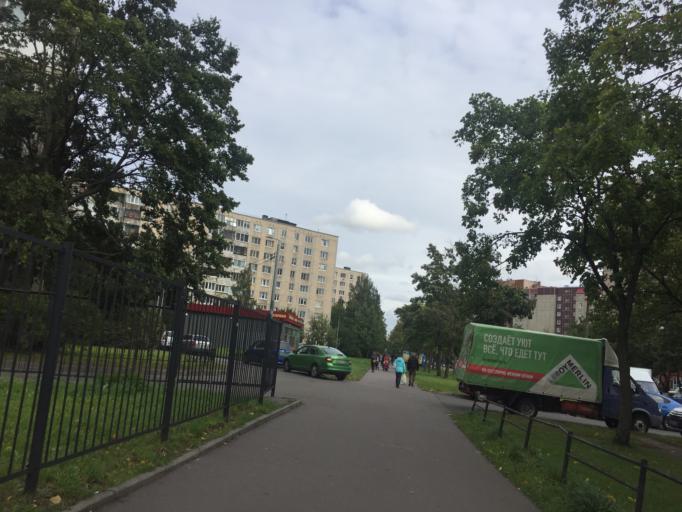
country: RU
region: St.-Petersburg
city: Shushary
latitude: 59.8288
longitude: 30.3876
